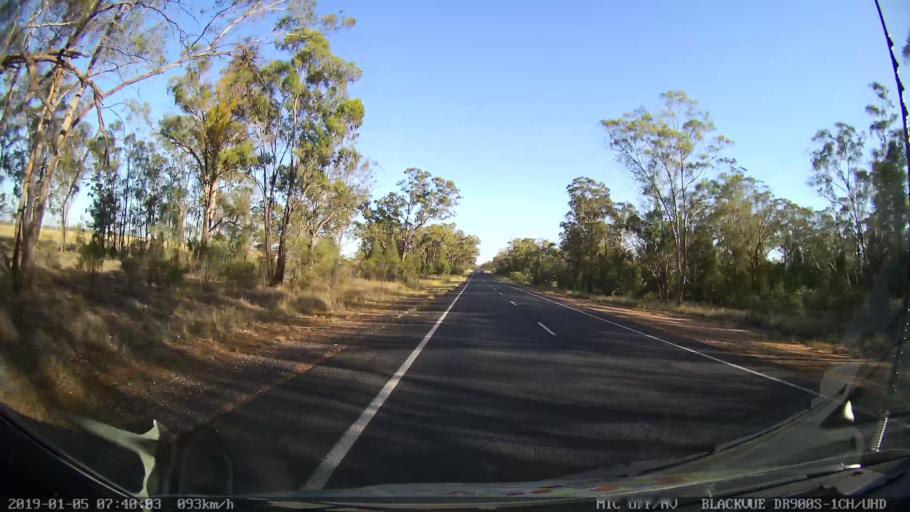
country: AU
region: New South Wales
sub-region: Gilgandra
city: Gilgandra
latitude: -31.9293
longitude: 148.6196
